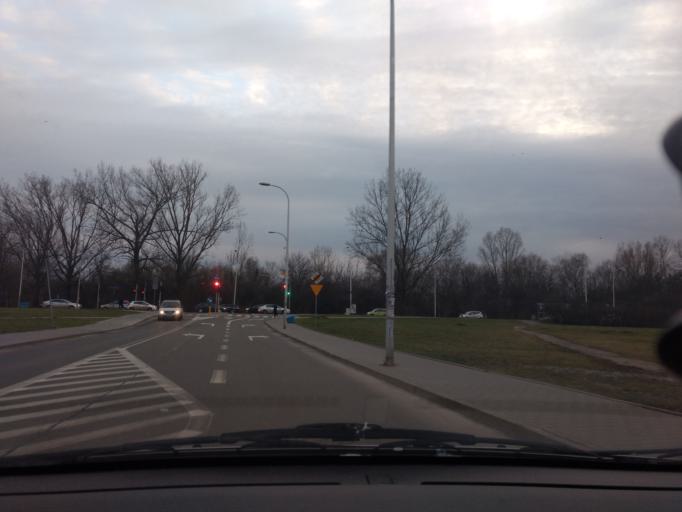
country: PL
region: Masovian Voivodeship
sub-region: Warszawa
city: Praga Poludnie
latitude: 52.2268
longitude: 21.0775
